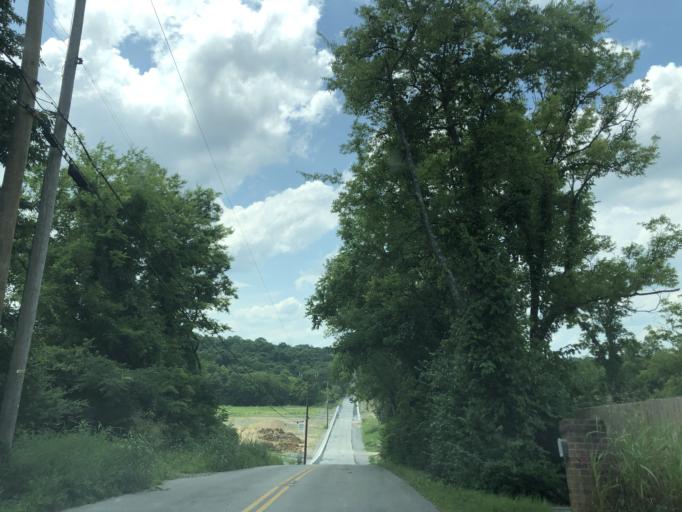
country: US
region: Tennessee
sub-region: Williamson County
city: Brentwood Estates
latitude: 36.0233
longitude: -86.7309
